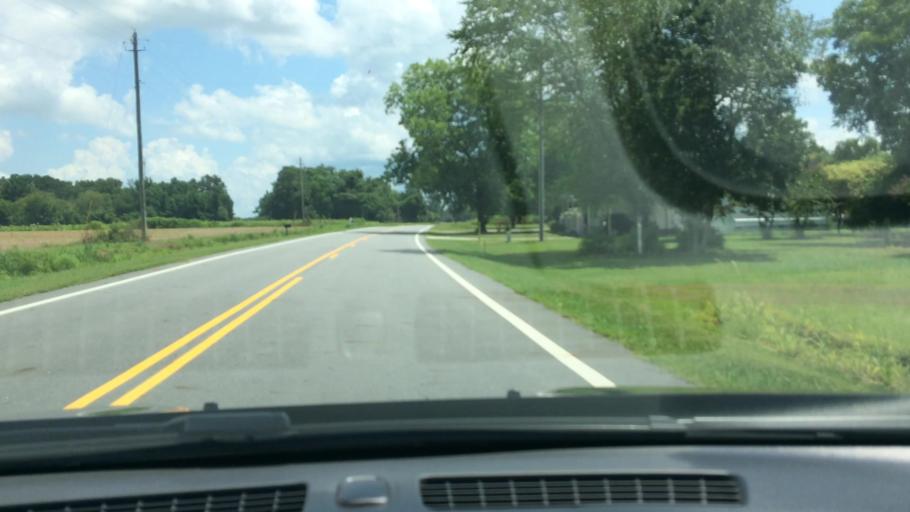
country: US
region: North Carolina
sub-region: Craven County
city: Vanceboro
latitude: 35.4190
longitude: -77.2352
